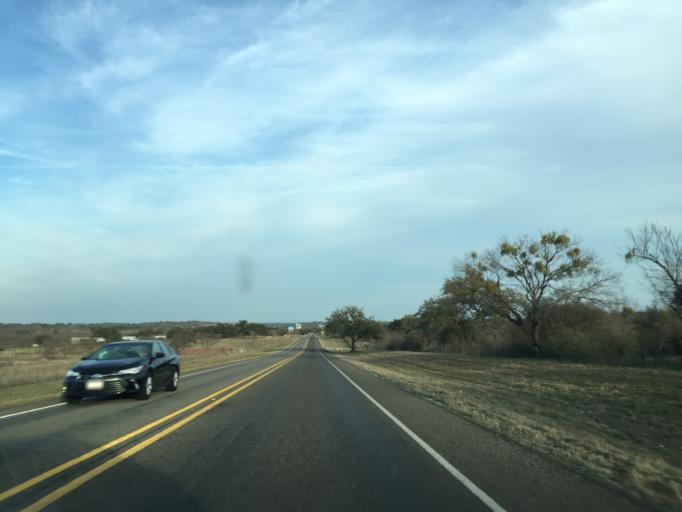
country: US
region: Texas
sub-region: Llano County
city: Llano
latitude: 30.7617
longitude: -98.6422
